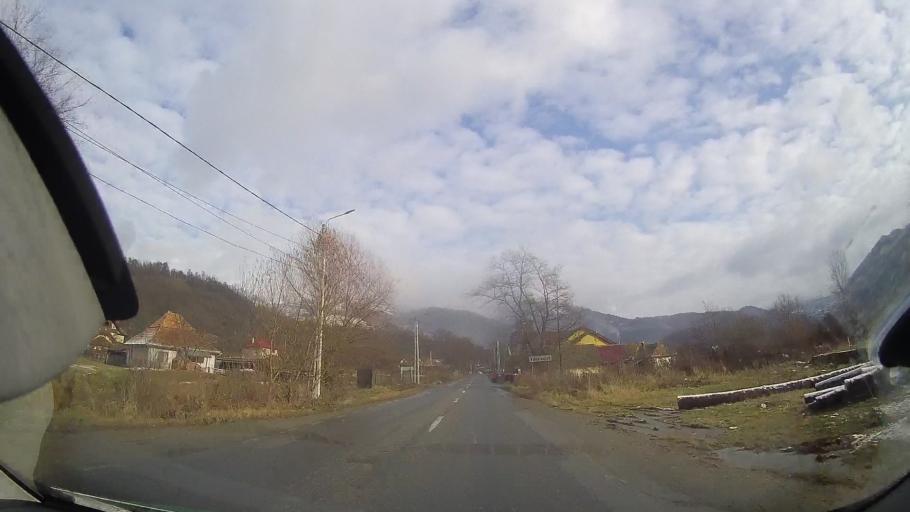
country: RO
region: Alba
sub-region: Comuna Lupsa
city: Lupsa
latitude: 46.3766
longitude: 23.2185
